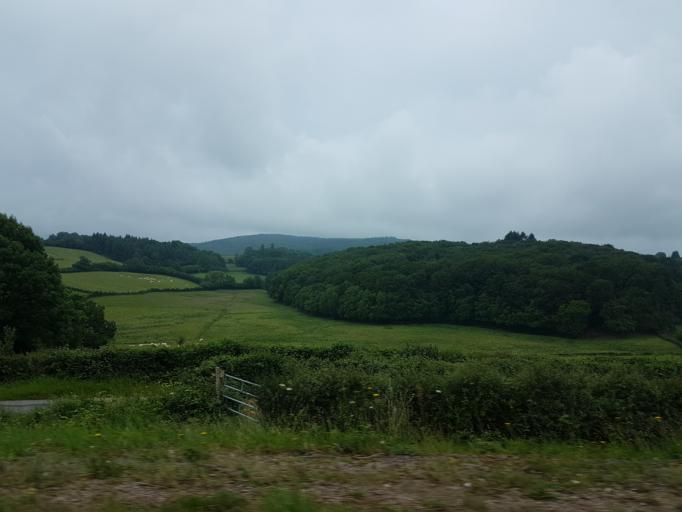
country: FR
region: Bourgogne
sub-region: Departement de la Nievre
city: Chateau-Chinon(Ville)
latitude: 47.0490
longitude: 3.9474
